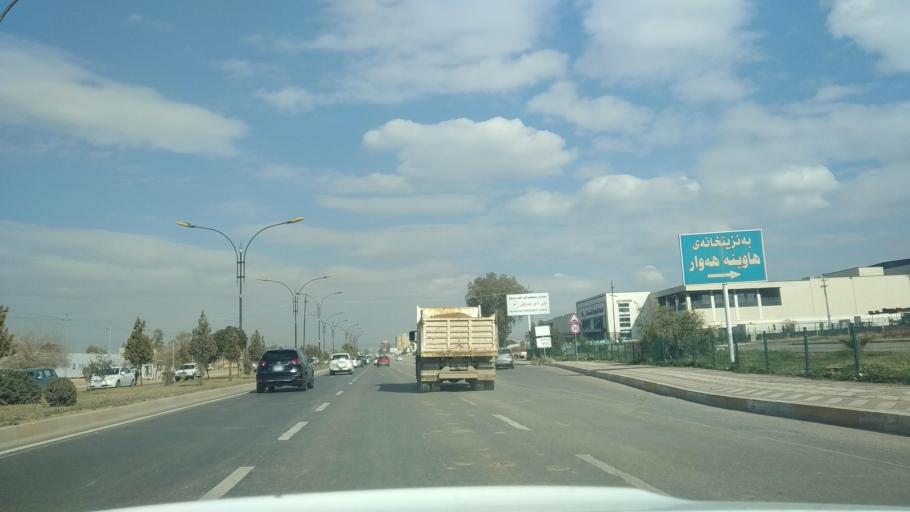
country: IQ
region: Arbil
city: Erbil
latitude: 36.2523
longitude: 44.0782
